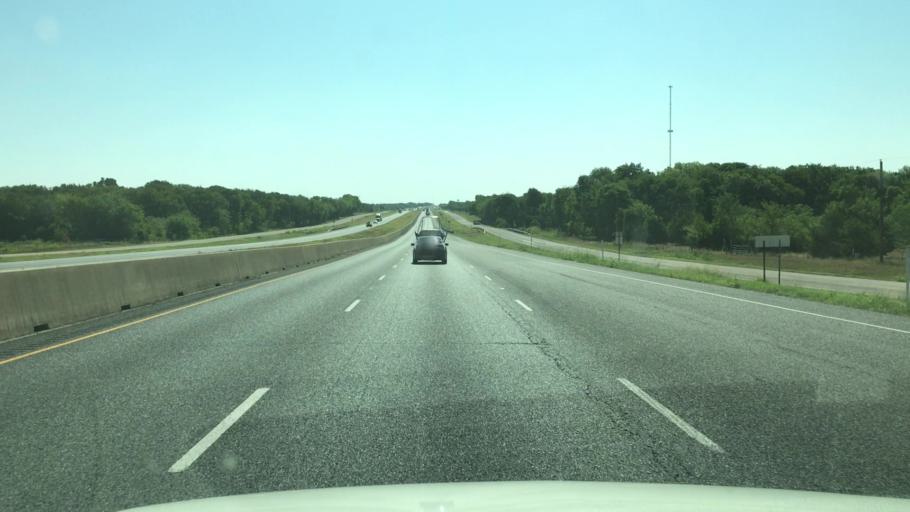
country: US
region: Texas
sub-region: Hunt County
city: Commerce
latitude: 33.1317
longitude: -95.9358
